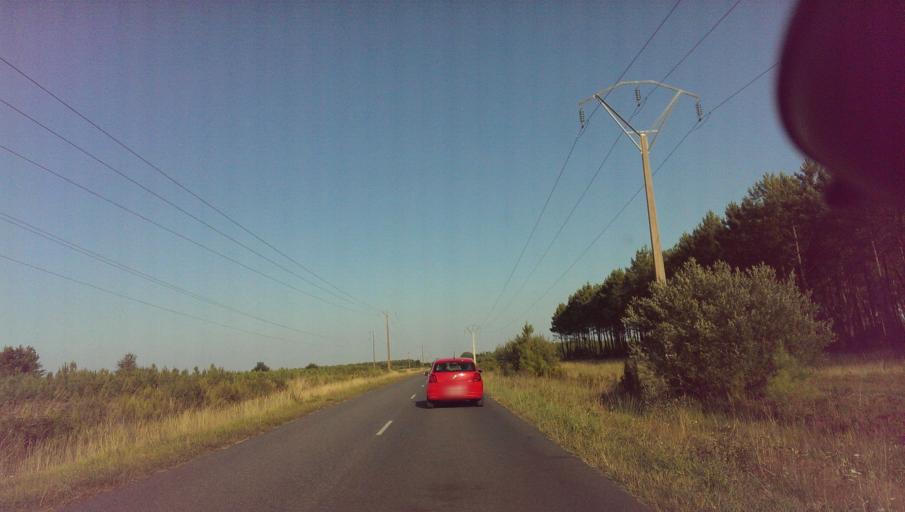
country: FR
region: Aquitaine
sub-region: Departement des Landes
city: Mimizan
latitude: 44.1848
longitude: -1.1932
